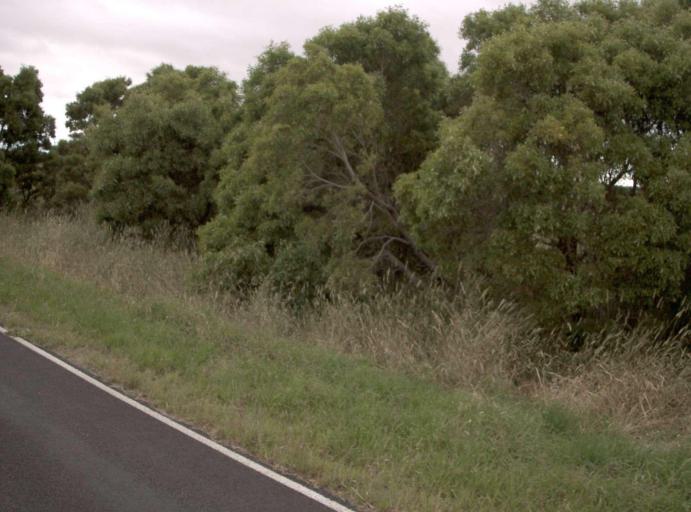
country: AU
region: Victoria
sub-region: Wellington
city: Sale
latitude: -38.5494
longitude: 146.8854
